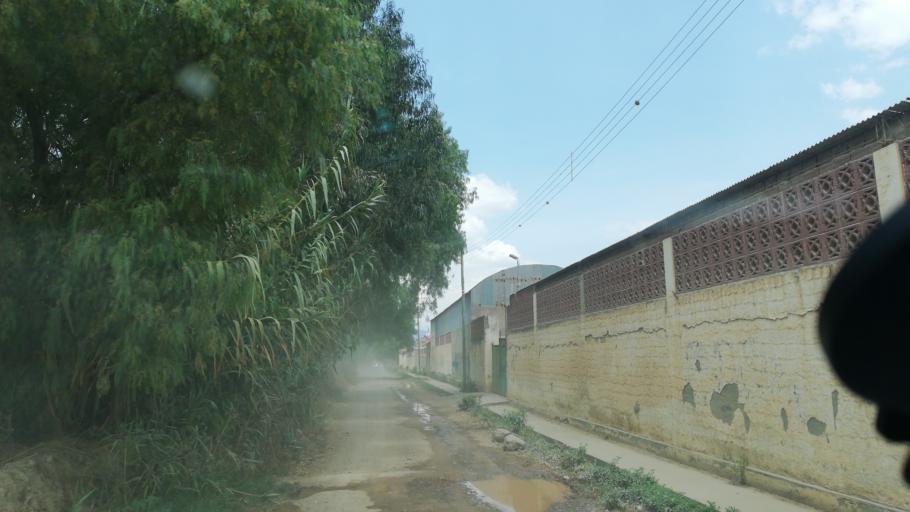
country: BO
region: Cochabamba
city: Cochabamba
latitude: -17.3599
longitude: -66.2220
